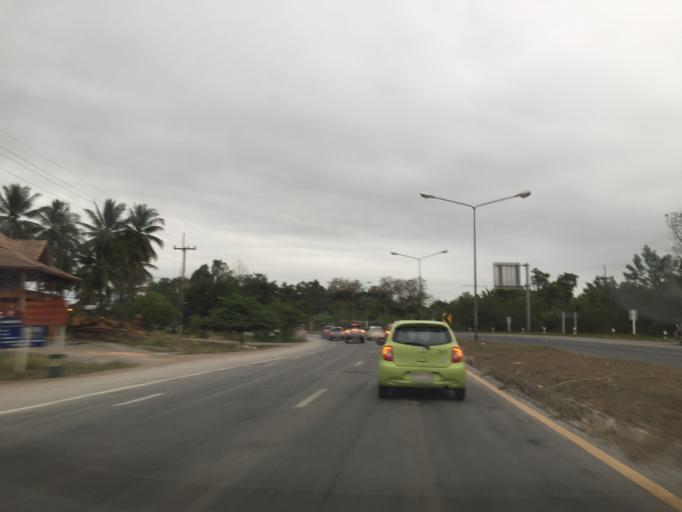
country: TH
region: Loei
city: Erawan
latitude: 17.2990
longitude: 101.9577
